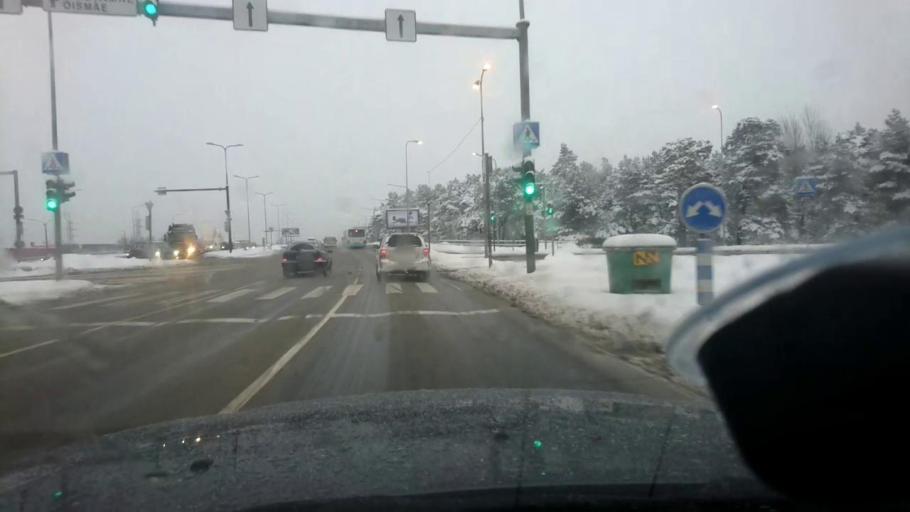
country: EE
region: Harju
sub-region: Tallinna linn
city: Tallinn
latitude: 59.3934
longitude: 24.7245
